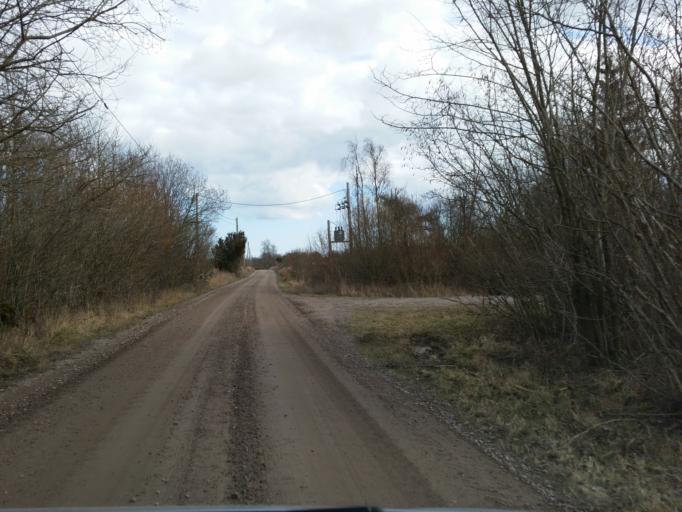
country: SE
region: Kalmar
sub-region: Morbylanga Kommun
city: Sodra Sandby
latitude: 56.6778
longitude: 16.6041
